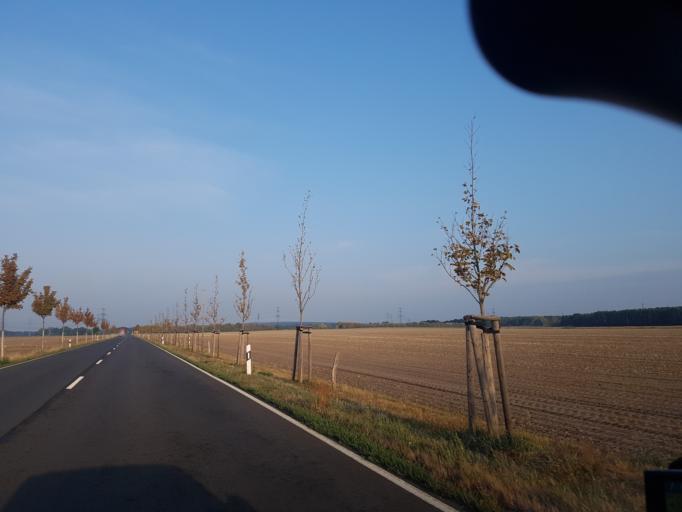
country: DE
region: Saxony-Anhalt
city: Annaburg
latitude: 51.7870
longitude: 13.0664
